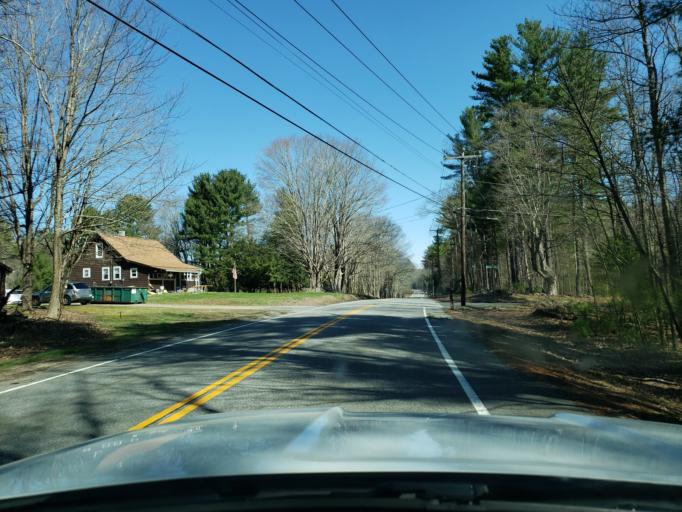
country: US
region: Connecticut
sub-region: Windham County
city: South Woodstock
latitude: 41.9580
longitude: -72.0788
